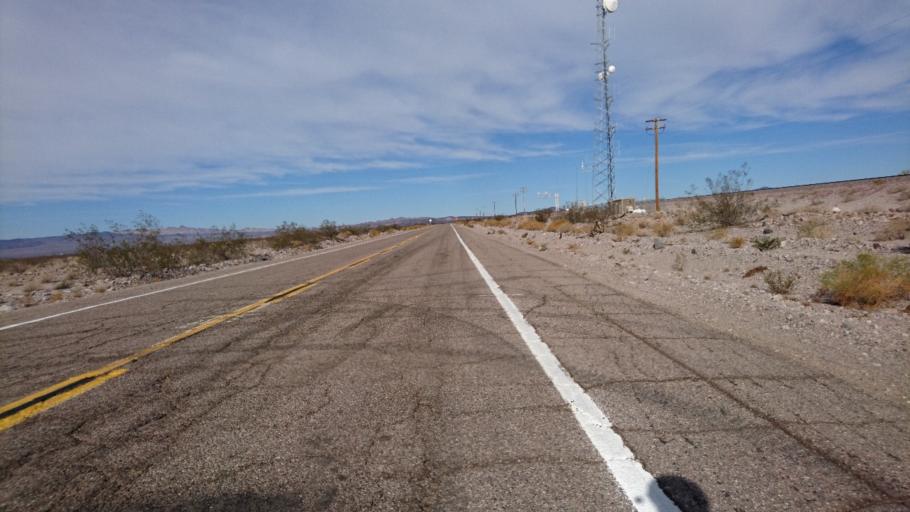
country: US
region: California
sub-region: San Bernardino County
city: Twentynine Palms
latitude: 34.6051
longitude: -115.9610
